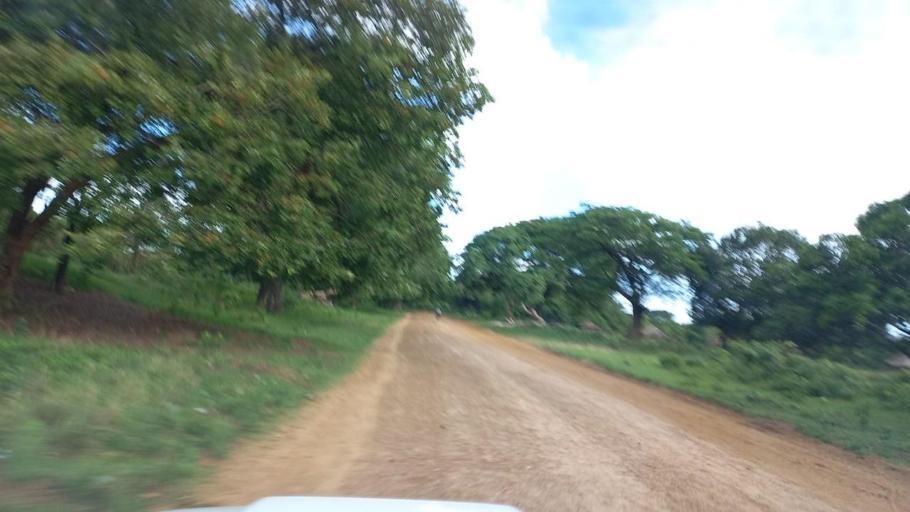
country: ZM
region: North-Western
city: Kabompo
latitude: -13.3763
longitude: 24.2996
